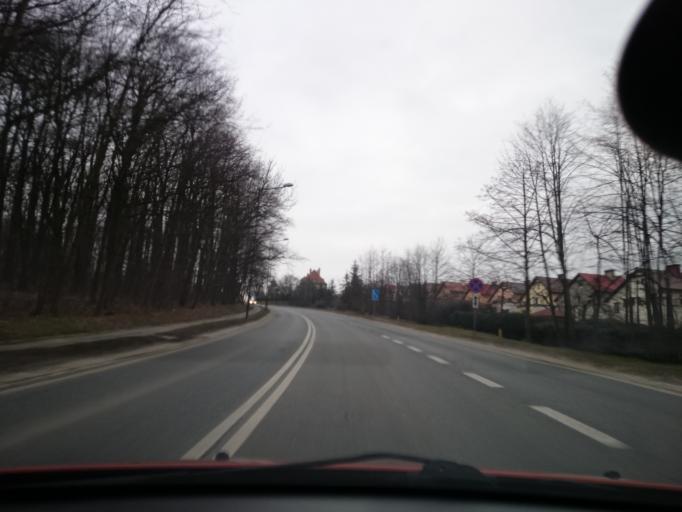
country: PL
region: Opole Voivodeship
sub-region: Powiat nyski
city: Nysa
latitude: 50.4811
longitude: 17.3080
